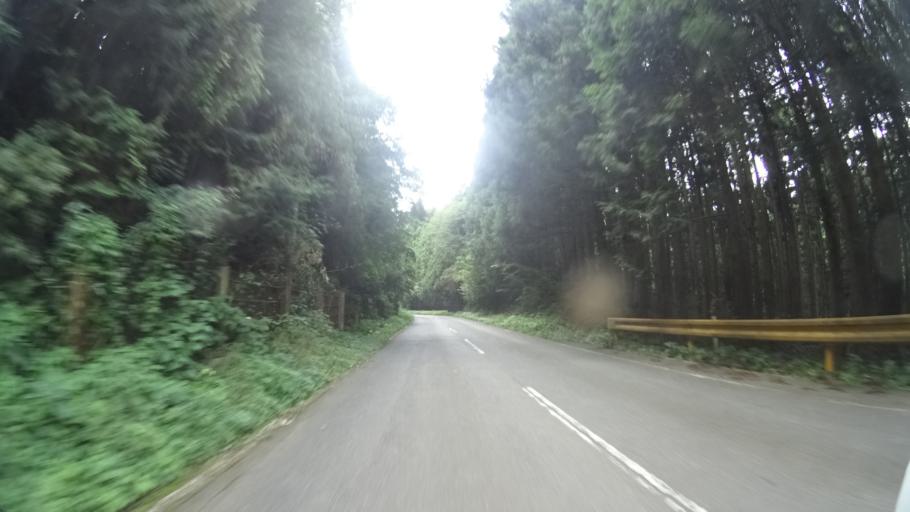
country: JP
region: Yamaguchi
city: Hagi
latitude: 34.5072
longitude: 131.5870
